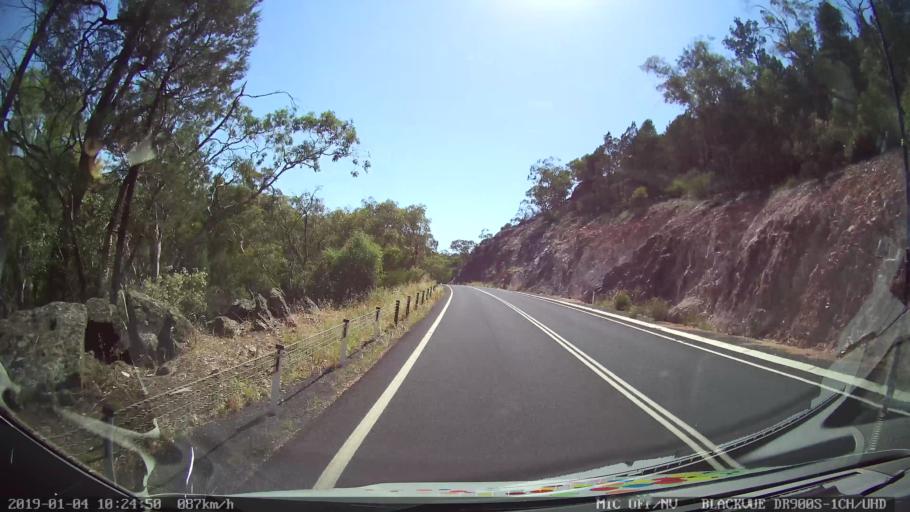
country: AU
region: New South Wales
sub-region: Cabonne
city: Canowindra
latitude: -33.3696
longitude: 148.5613
